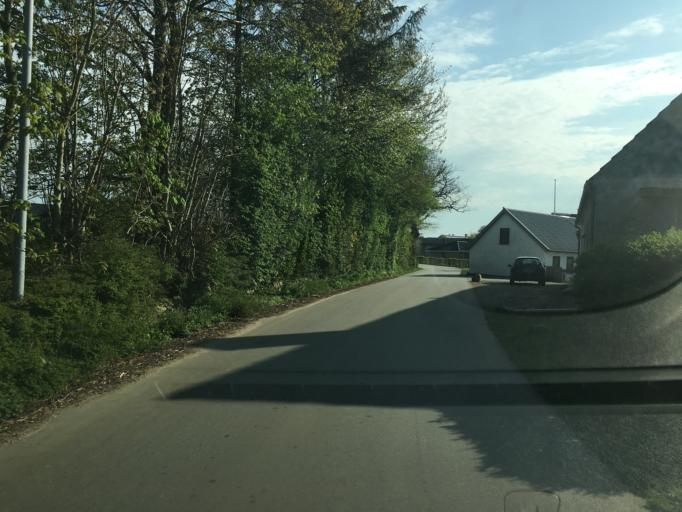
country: DK
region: South Denmark
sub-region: Haderslev Kommune
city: Vojens
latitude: 55.1684
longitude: 9.3807
